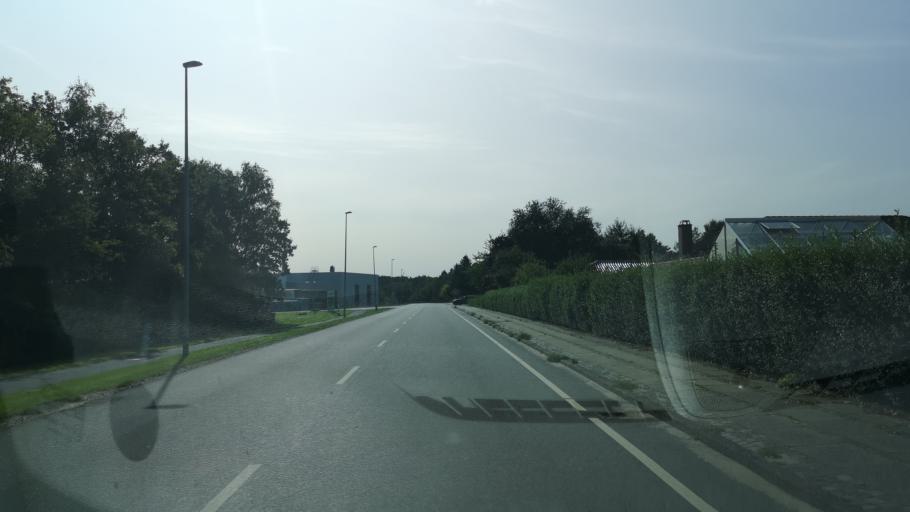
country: DK
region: Central Jutland
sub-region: Ringkobing-Skjern Kommune
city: Videbaek
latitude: 56.0857
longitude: 8.6285
